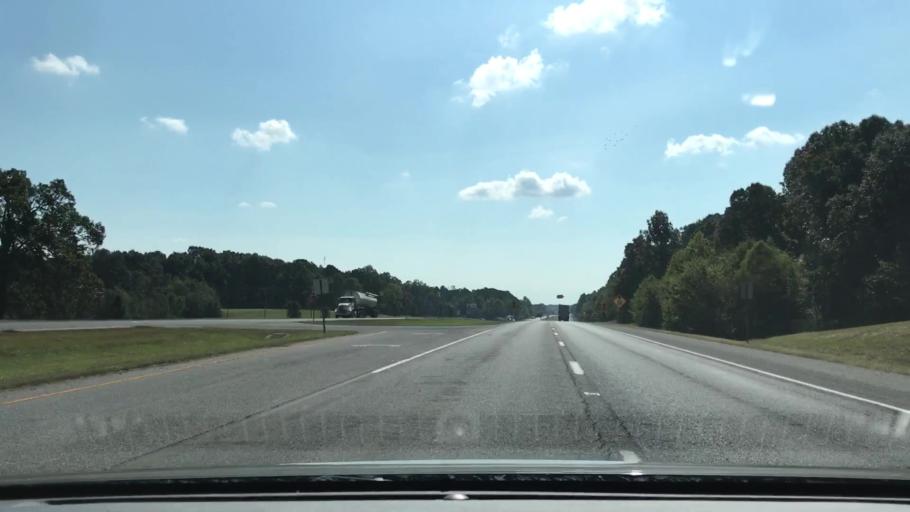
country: US
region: Kentucky
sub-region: Marshall County
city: Benton
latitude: 36.7695
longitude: -88.3144
